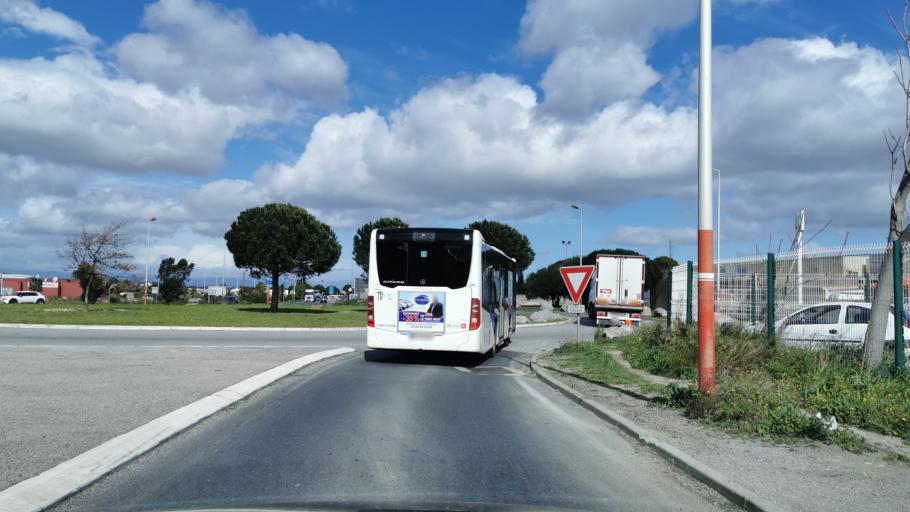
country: FR
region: Languedoc-Roussillon
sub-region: Departement de l'Aude
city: Narbonne
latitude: 43.1621
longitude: 2.9889
